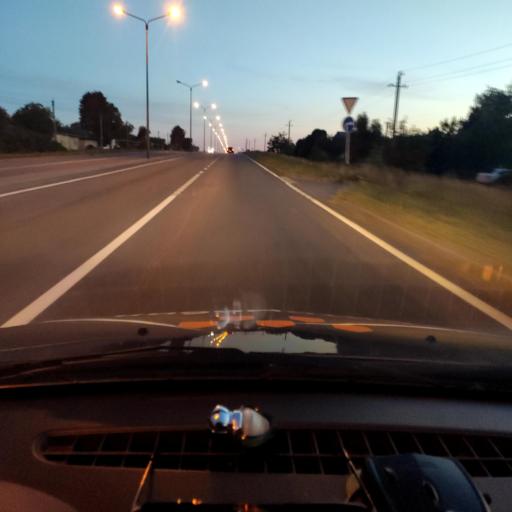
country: RU
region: Belgorod
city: Gubkin
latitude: 51.2660
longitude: 37.5556
